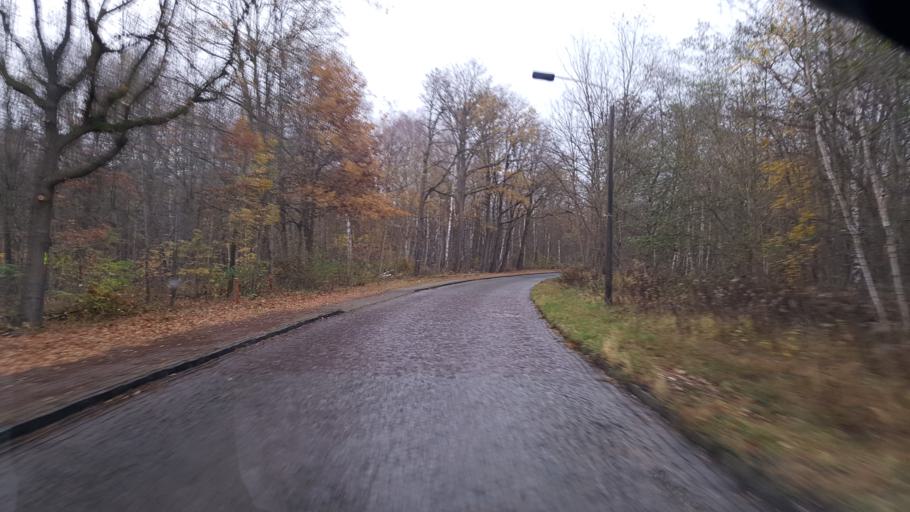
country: DE
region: Brandenburg
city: Lauchhammer
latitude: 51.4935
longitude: 13.7371
